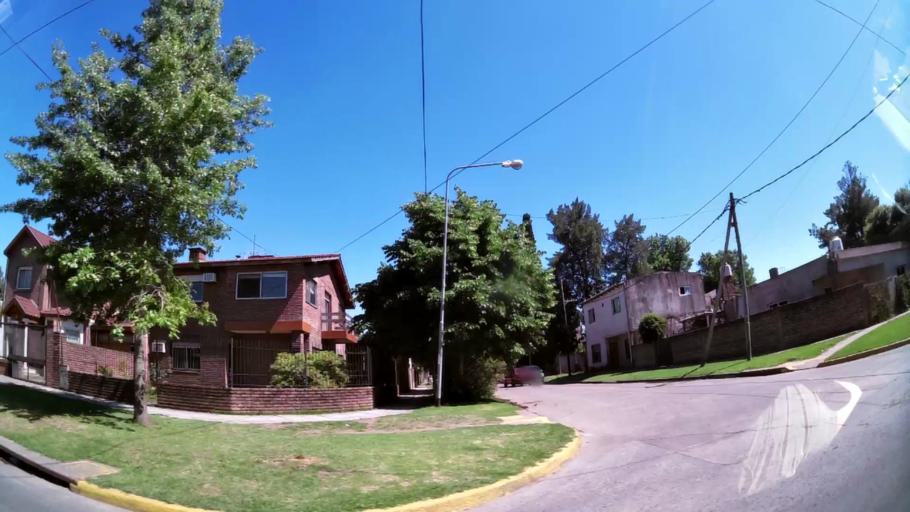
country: AR
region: Buenos Aires
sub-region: Partido de Tigre
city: Tigre
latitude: -34.4987
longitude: -58.6270
